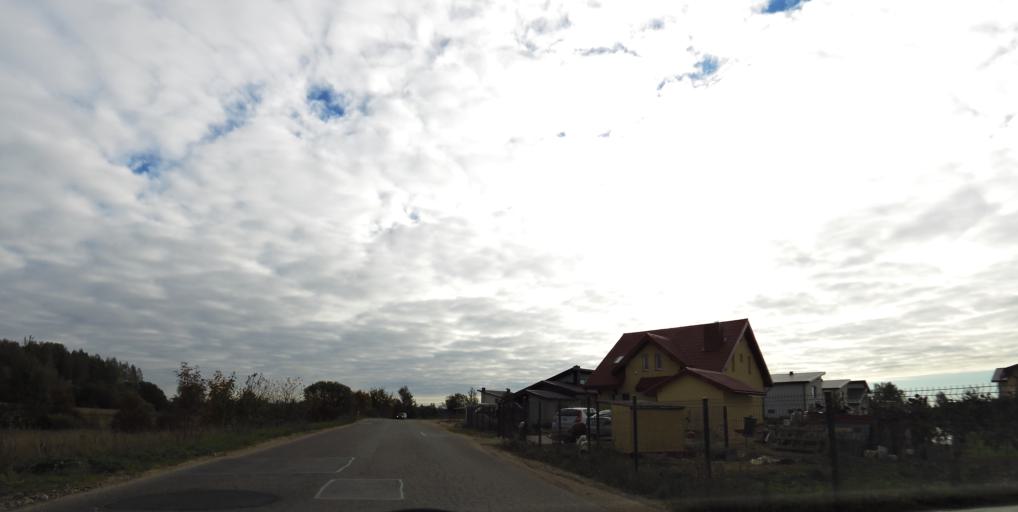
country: LT
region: Vilnius County
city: Pilaite
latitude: 54.7219
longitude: 25.1550
